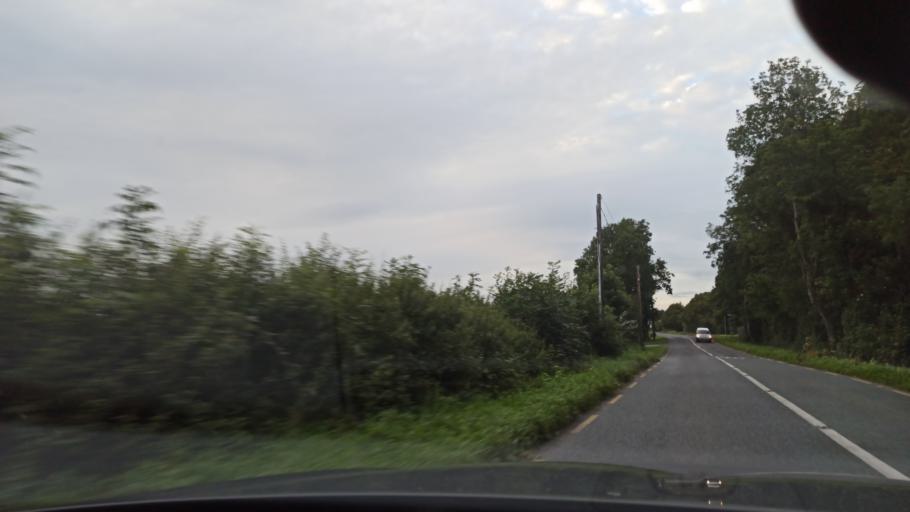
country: IE
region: Munster
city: Cashel
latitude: 52.4893
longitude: -7.8584
